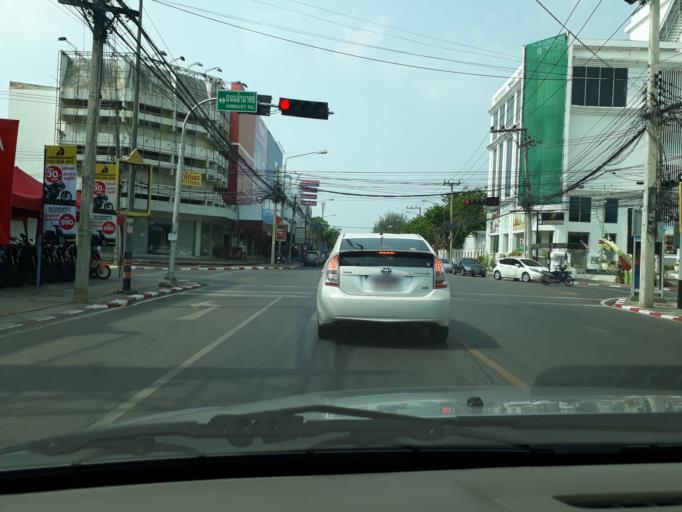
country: TH
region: Khon Kaen
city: Khon Kaen
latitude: 16.4338
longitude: 102.8363
